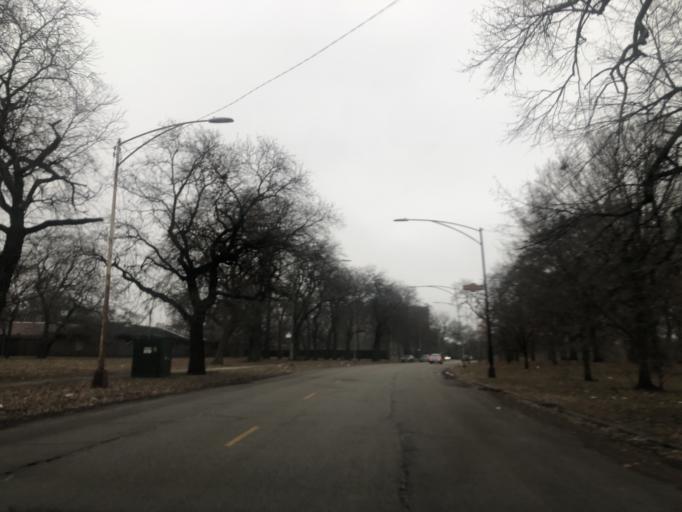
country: US
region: Illinois
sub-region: Cook County
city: Chicago
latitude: 41.7903
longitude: -87.6078
